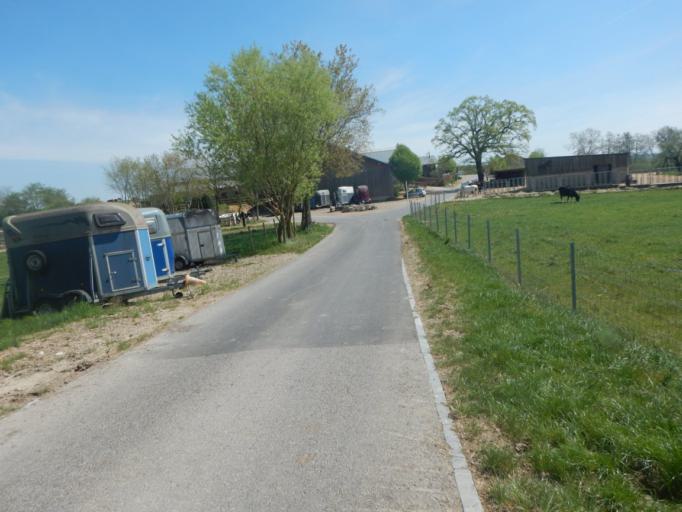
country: LU
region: Diekirch
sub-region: Canton de Redange
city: Redange-sur-Attert
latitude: 49.7546
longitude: 5.9141
